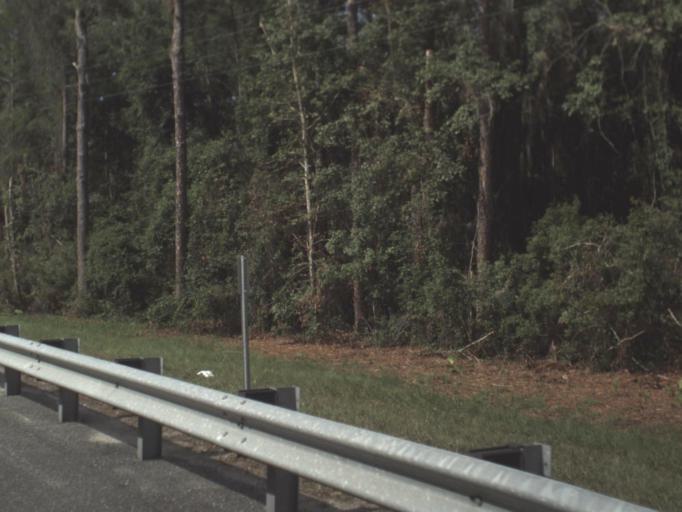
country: US
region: Florida
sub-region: Taylor County
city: Perry
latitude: 30.2536
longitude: -83.6233
